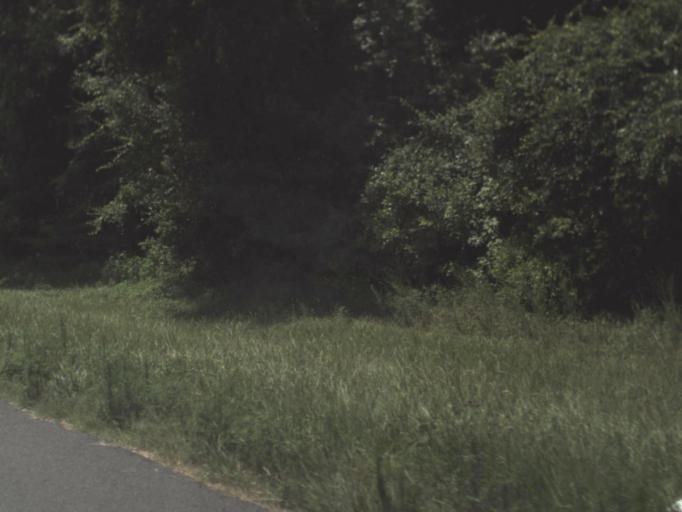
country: US
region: Florida
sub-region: Suwannee County
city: Wellborn
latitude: 30.3522
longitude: -82.7759
